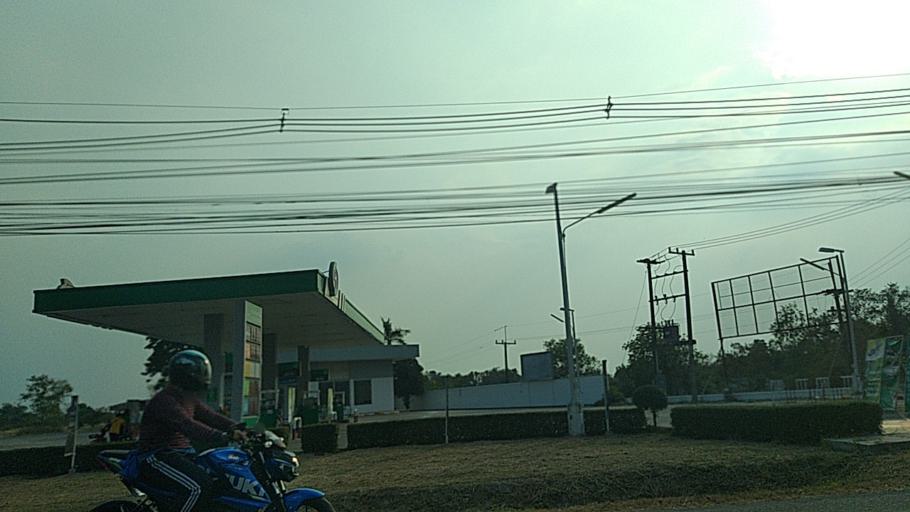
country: TH
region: Nakhon Nayok
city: Nakhon Nayok
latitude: 14.2095
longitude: 101.1802
